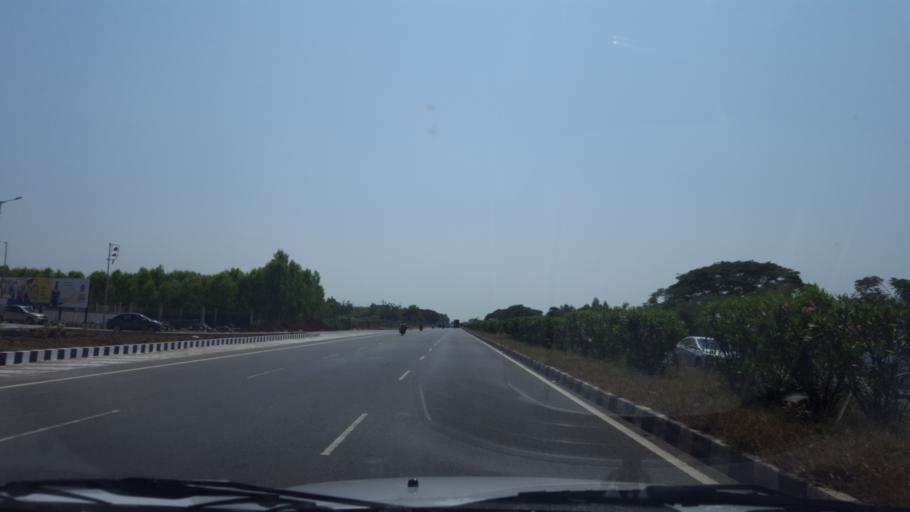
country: IN
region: Andhra Pradesh
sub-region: Prakasam
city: Ongole
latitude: 15.5971
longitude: 80.0328
